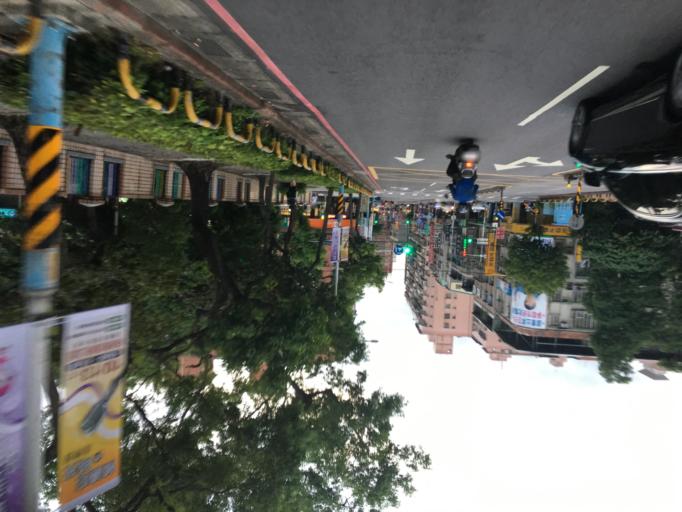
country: TW
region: Taipei
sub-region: Taipei
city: Banqiao
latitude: 24.9891
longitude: 121.4303
